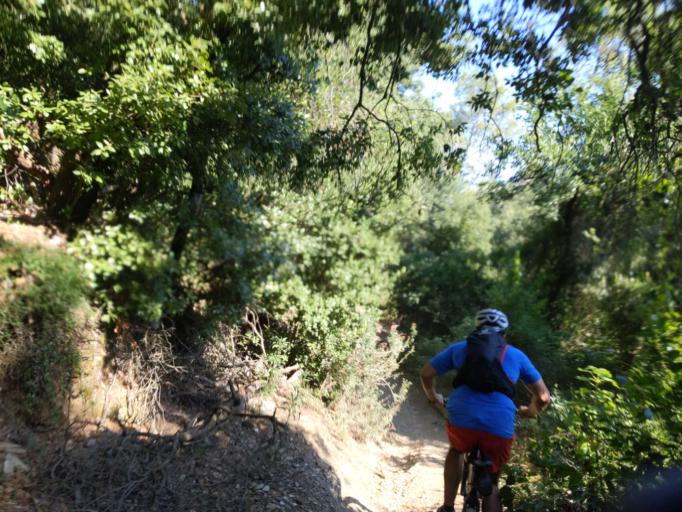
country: ES
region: Catalonia
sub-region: Provincia de Barcelona
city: Cerdanyola del Valles
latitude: 41.4661
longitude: 2.1330
